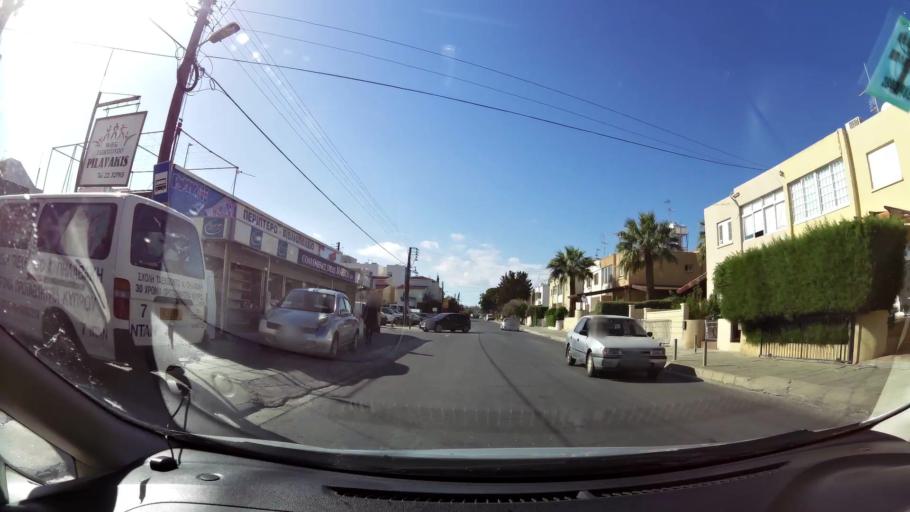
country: CY
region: Lefkosia
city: Nicosia
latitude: 35.1310
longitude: 33.3340
